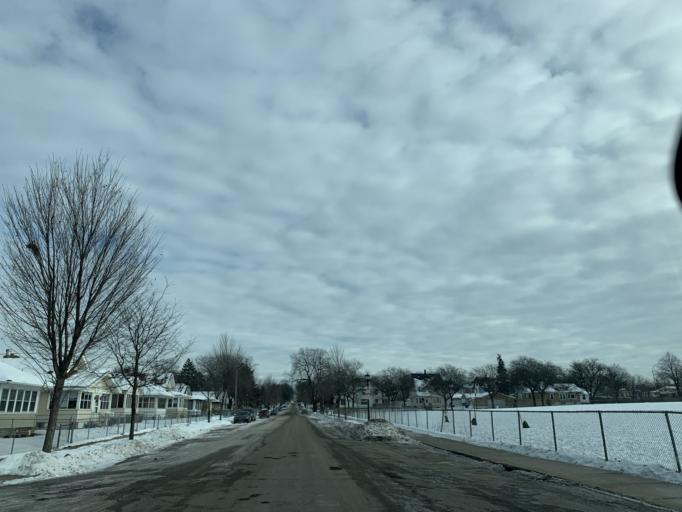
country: US
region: Minnesota
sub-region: Ramsey County
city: Saint Paul
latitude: 44.9530
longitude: -93.1350
